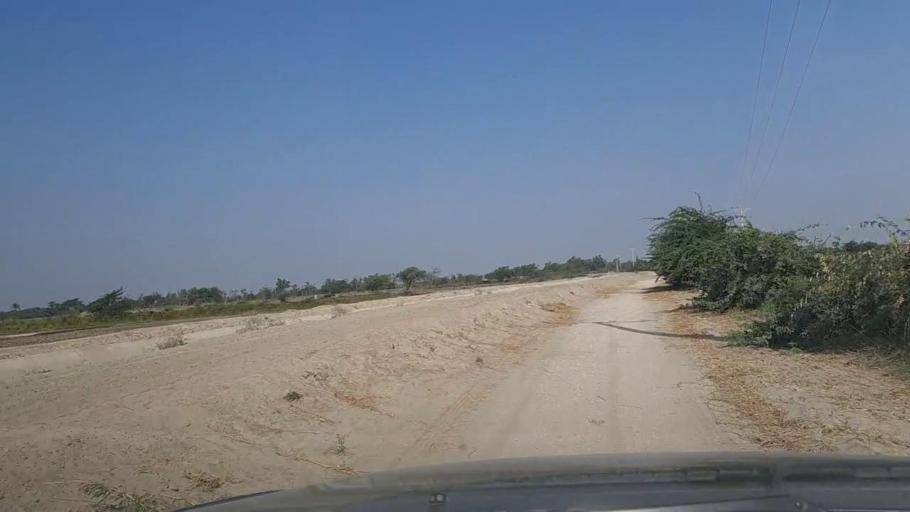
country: PK
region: Sindh
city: Mirpur Sakro
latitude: 24.5138
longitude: 67.8045
